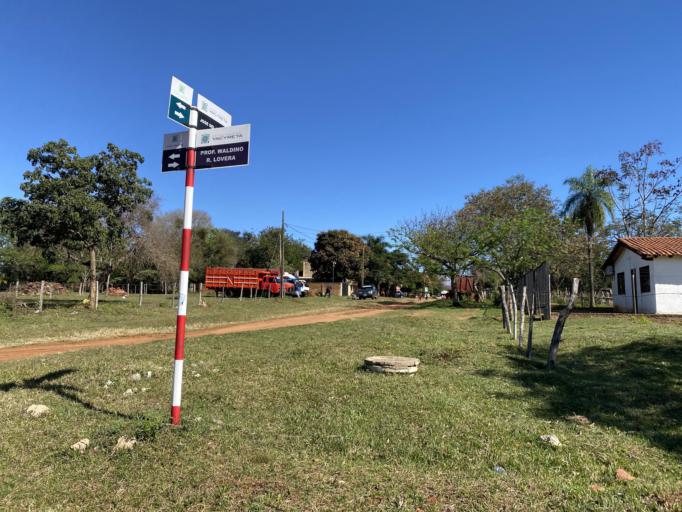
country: PY
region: Misiones
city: San Juan Bautista
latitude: -26.6742
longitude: -57.1412
